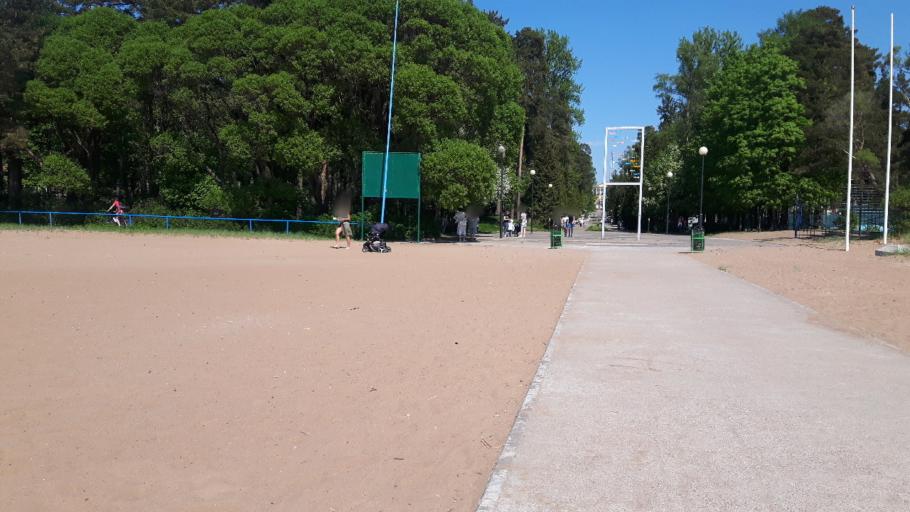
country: RU
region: St.-Petersburg
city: Zelenogorsk
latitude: 60.1881
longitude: 29.6998
